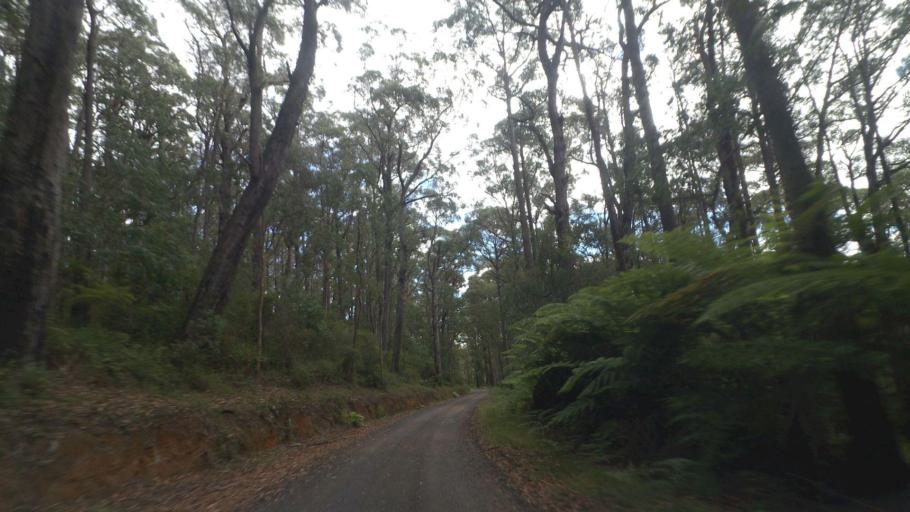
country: AU
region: Victoria
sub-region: Cardinia
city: Gembrook
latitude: -37.8934
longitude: 145.6551
